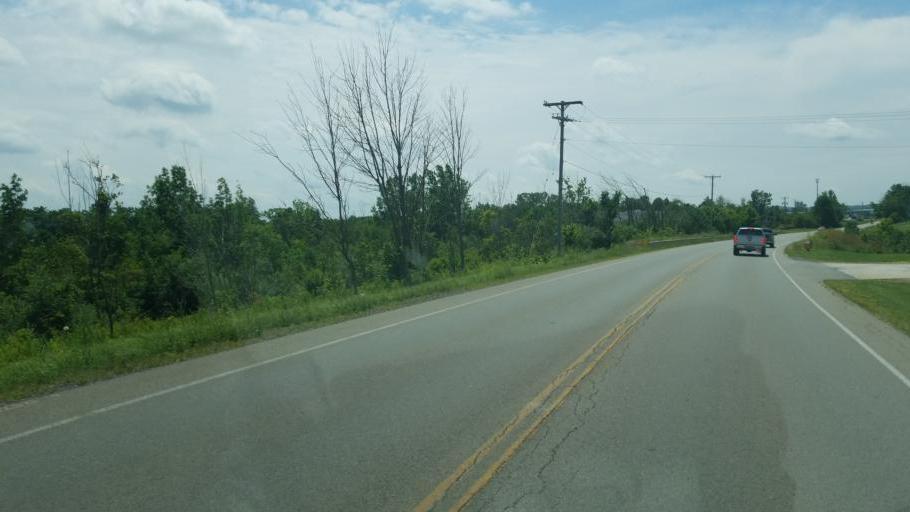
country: US
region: Ohio
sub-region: Richland County
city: Lincoln Heights
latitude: 40.8060
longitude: -82.5018
